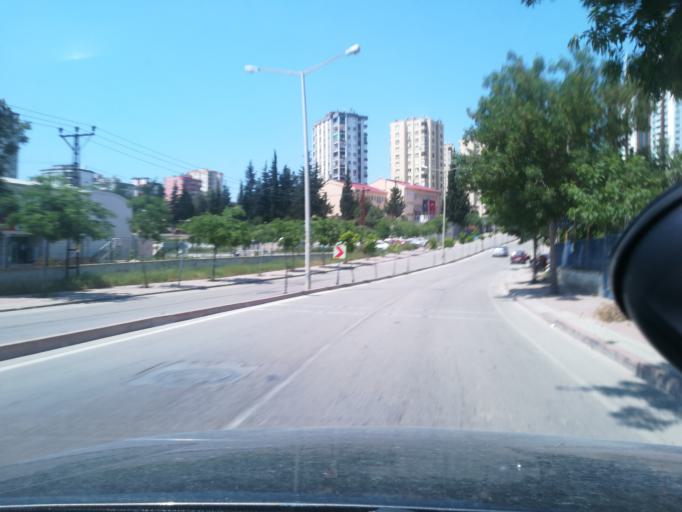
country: TR
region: Adana
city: Seyhan
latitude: 37.0335
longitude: 35.2677
